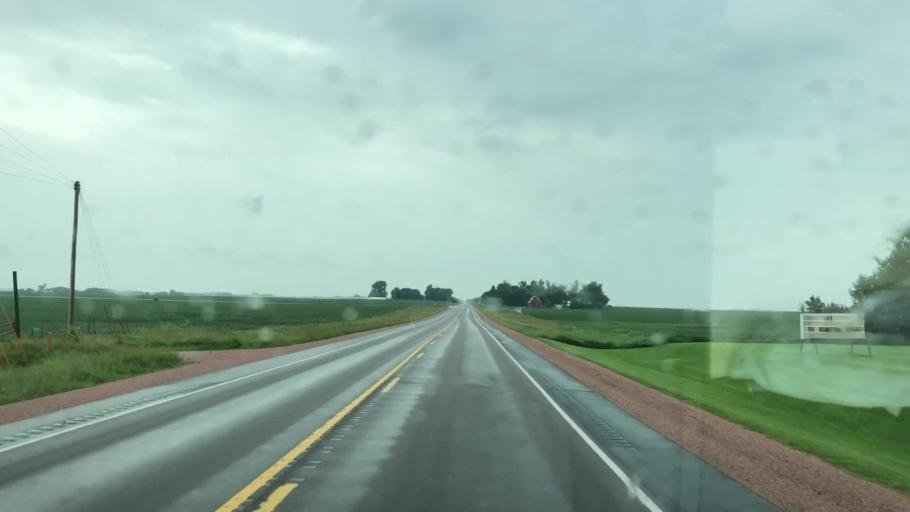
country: US
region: Iowa
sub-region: O'Brien County
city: Sanborn
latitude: 43.1862
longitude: -95.7372
